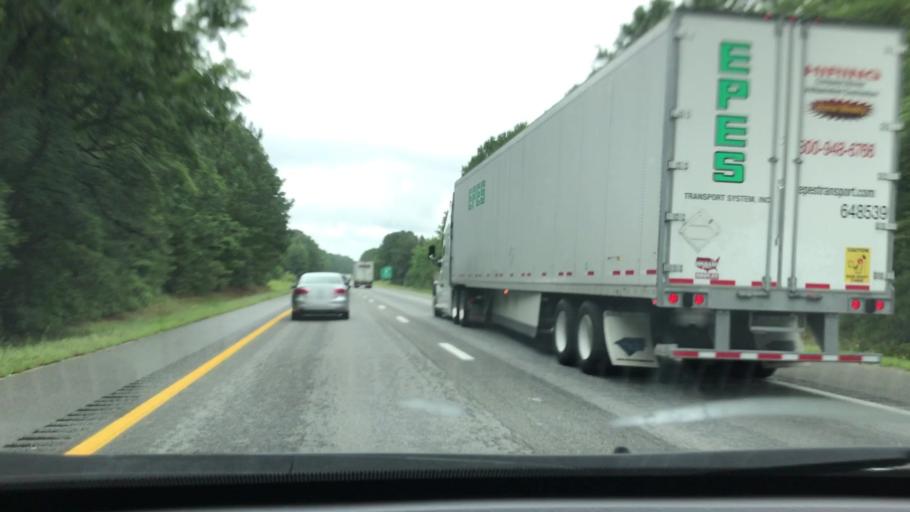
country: US
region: Virginia
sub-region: City of Emporia
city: Emporia
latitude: 36.7842
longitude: -77.4617
